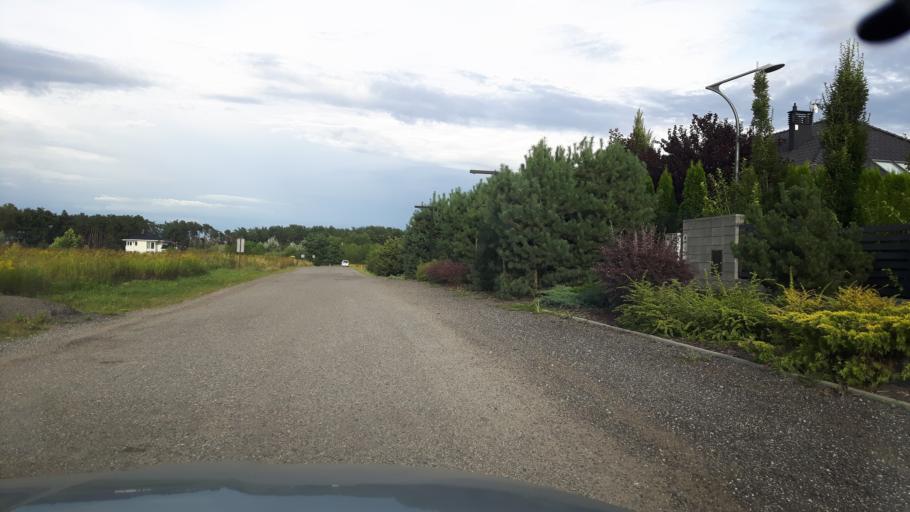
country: PL
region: Masovian Voivodeship
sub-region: Powiat wolominski
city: Marki
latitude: 52.3116
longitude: 21.0833
